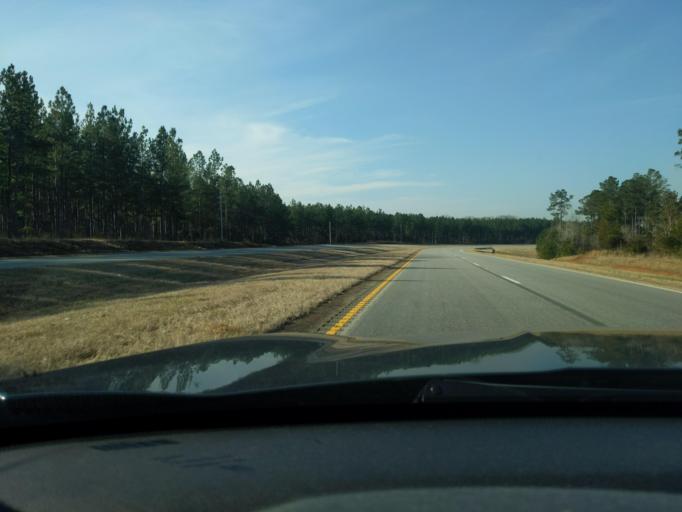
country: US
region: South Carolina
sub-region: Abbeville County
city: Abbeville
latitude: 34.1144
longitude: -82.4666
